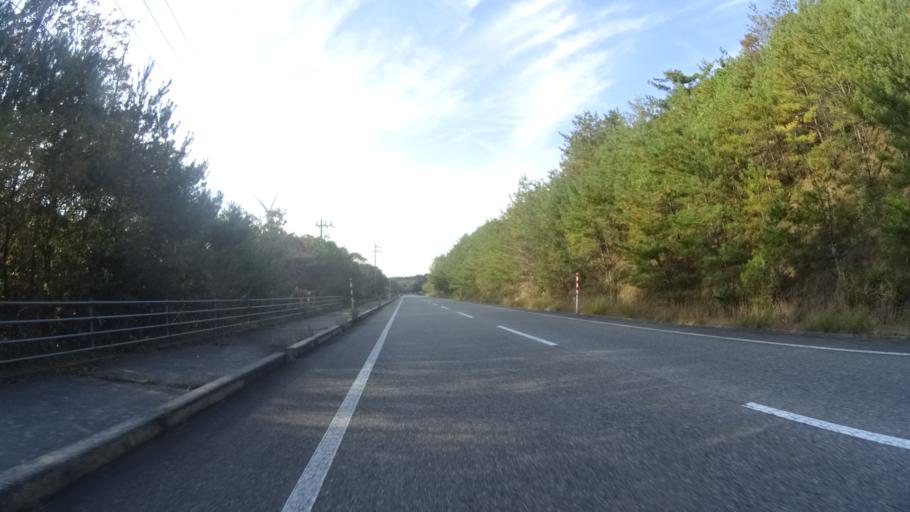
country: JP
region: Ishikawa
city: Hakui
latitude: 37.0718
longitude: 136.7354
